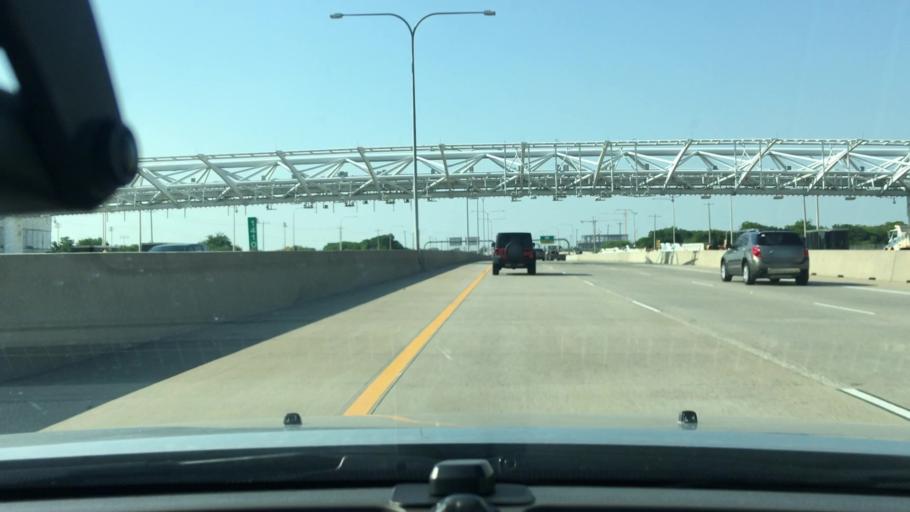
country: US
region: Texas
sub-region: Collin County
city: Frisco
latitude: 33.1634
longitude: -96.8400
